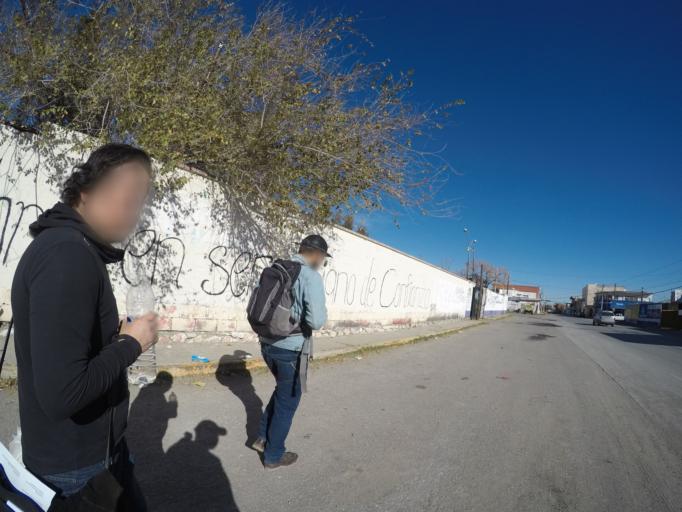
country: MX
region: Chihuahua
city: Ciudad Juarez
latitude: 31.7346
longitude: -106.4576
